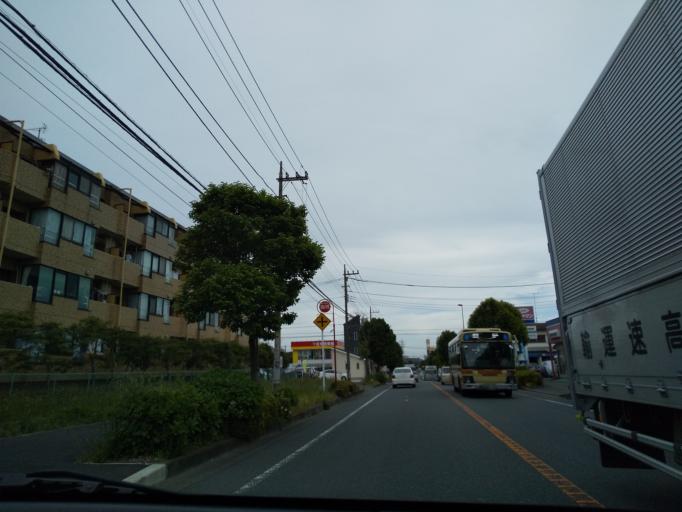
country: JP
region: Kanagawa
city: Zama
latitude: 35.5198
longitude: 139.4029
